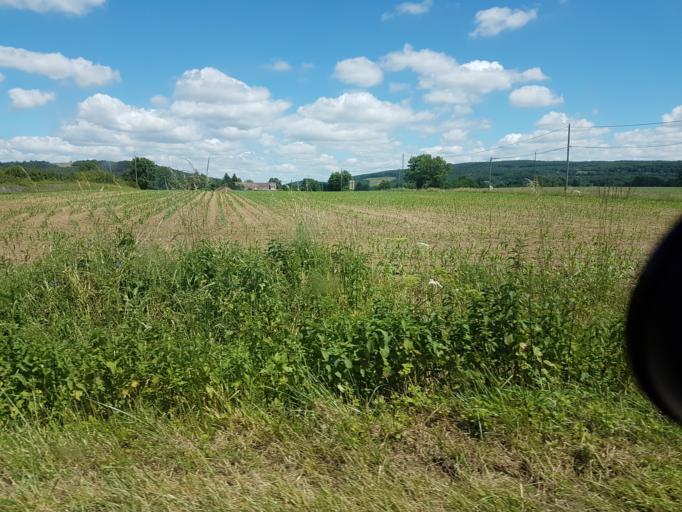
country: FR
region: Bourgogne
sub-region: Departement de Saone-et-Loire
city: Curgy
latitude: 47.0507
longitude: 4.3464
